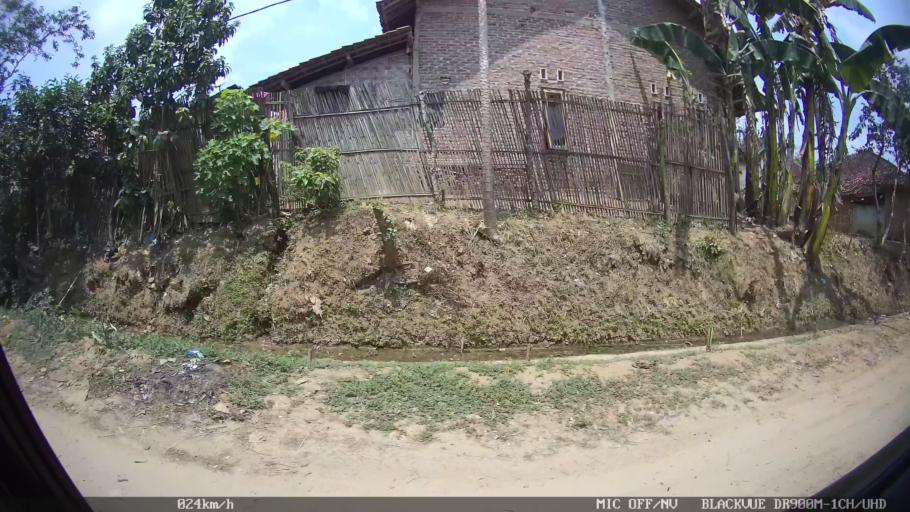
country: ID
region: Lampung
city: Pringsewu
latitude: -5.3413
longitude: 104.9849
